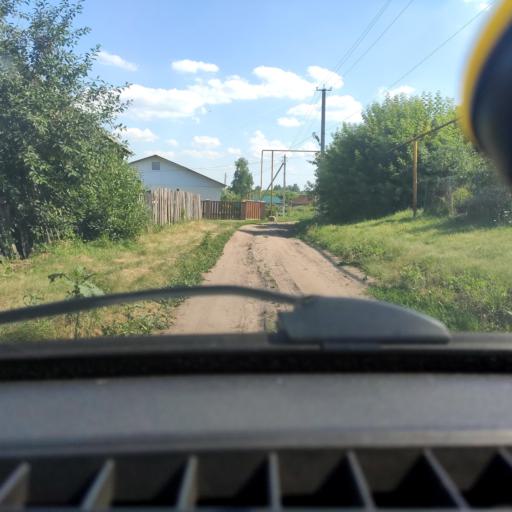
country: RU
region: Samara
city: Povolzhskiy
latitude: 53.7566
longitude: 49.7334
